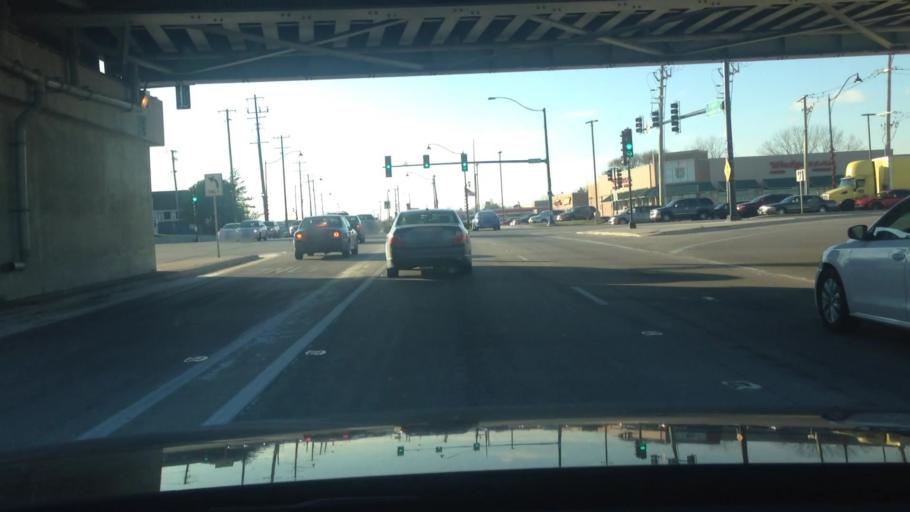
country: US
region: Illinois
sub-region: DuPage County
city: Bensenville
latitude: 41.9609
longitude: -87.9387
